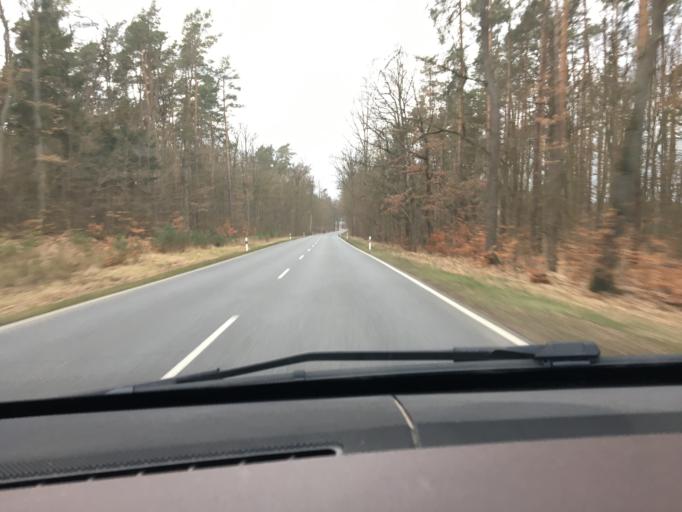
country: DE
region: Brandenburg
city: Liebenwalde
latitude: 52.8745
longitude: 13.4842
